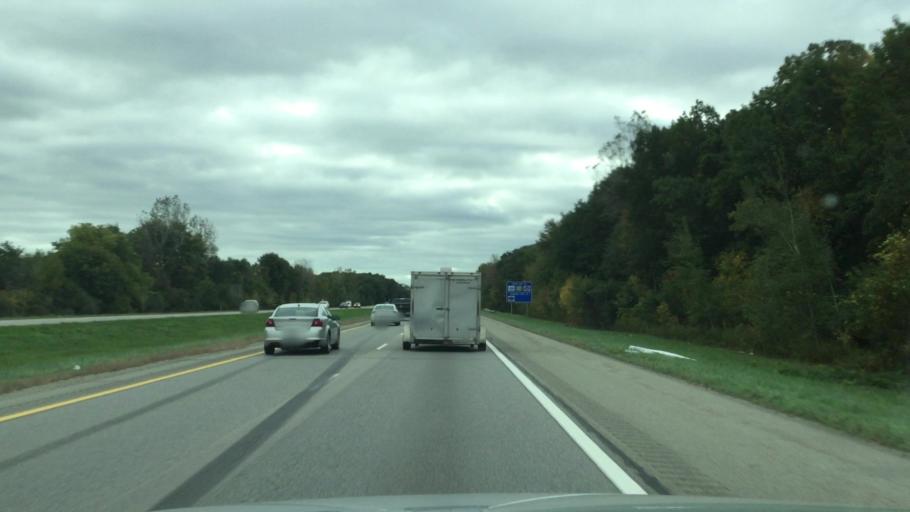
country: US
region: Michigan
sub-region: Macomb County
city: Shelby
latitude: 42.6920
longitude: -83.0212
